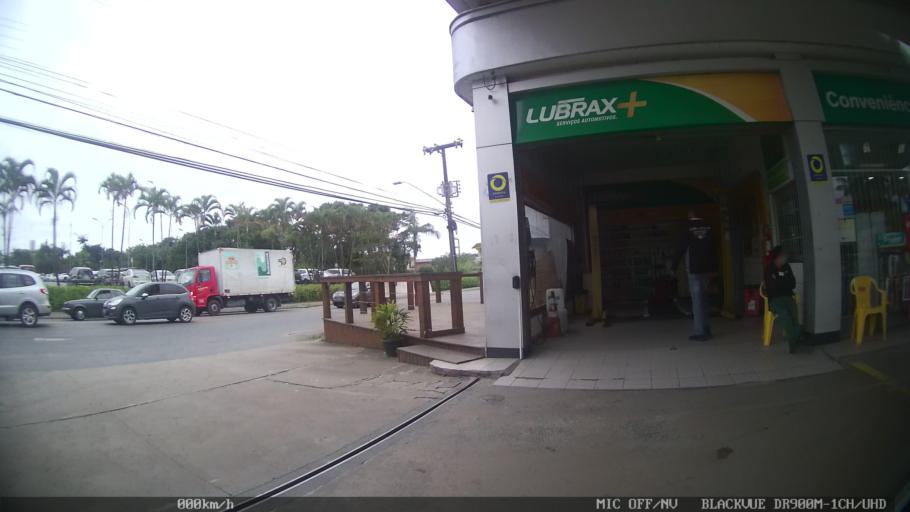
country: BR
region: Santa Catarina
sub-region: Joinville
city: Joinville
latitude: -26.2651
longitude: -48.8725
